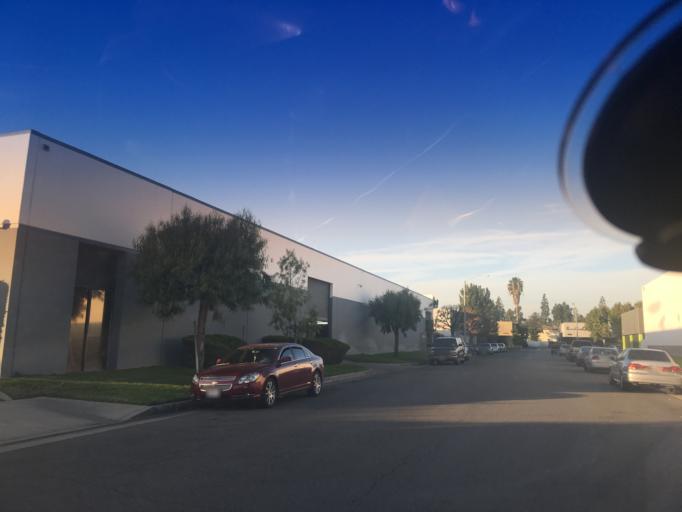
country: US
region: California
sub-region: Orange County
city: Anaheim
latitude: 33.8148
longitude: -117.8853
